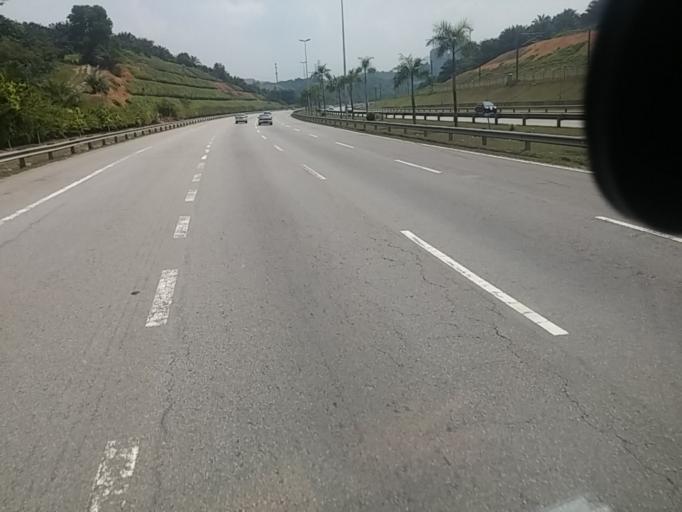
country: MY
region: Putrajaya
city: Putrajaya
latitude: 2.9481
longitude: 101.6602
